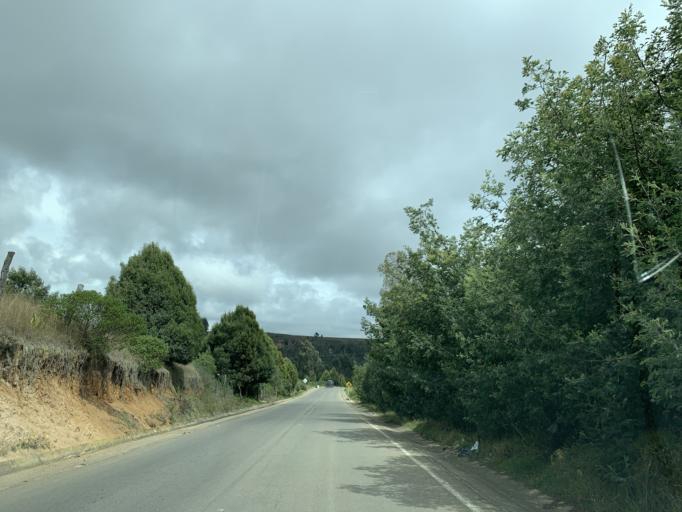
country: CO
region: Boyaca
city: Tunja
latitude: 5.5696
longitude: -73.3637
